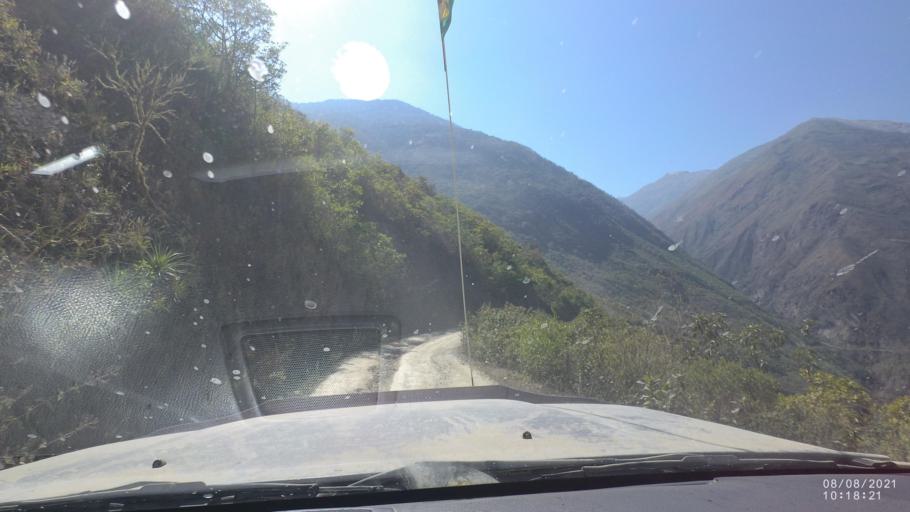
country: BO
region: La Paz
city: Quime
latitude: -16.6857
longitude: -66.7315
